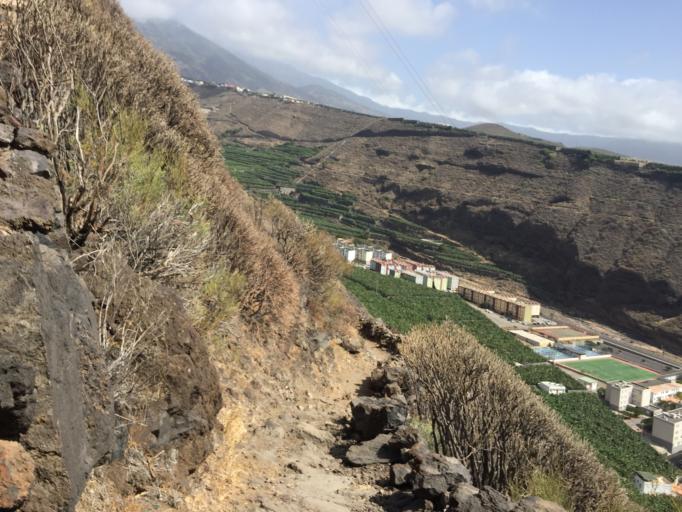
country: ES
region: Canary Islands
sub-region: Provincia de Santa Cruz de Tenerife
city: Tazacorte
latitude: 28.6534
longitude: -17.9480
